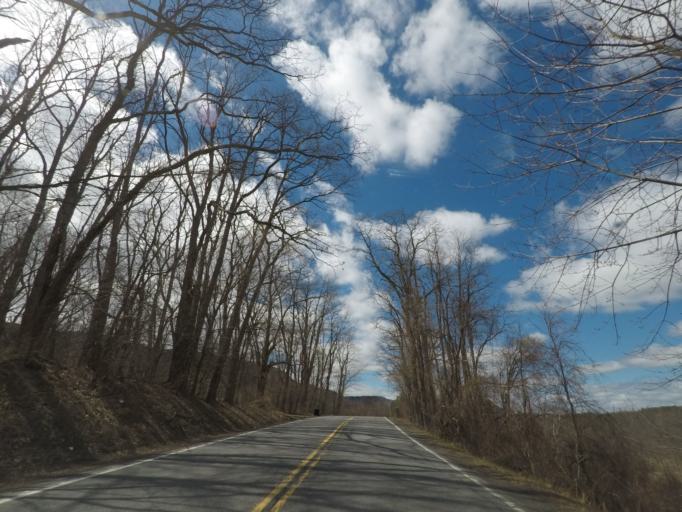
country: US
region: New York
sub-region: Albany County
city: Voorheesville
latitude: 42.6479
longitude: -73.9772
